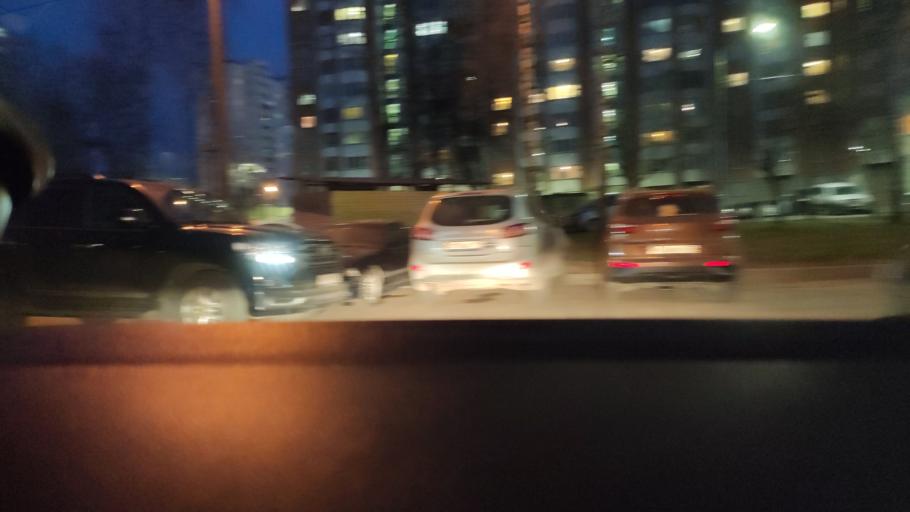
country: RU
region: Moscow
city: Nekrasovka
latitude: 55.6848
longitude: 37.9266
